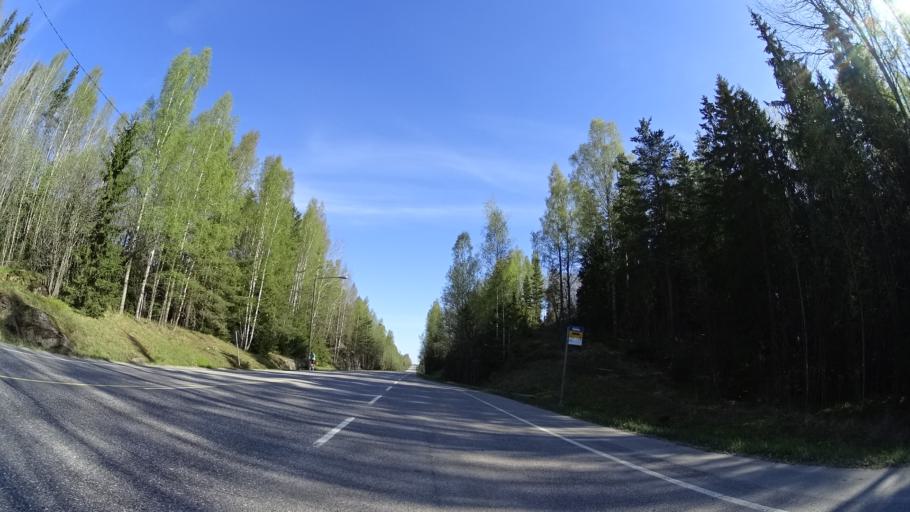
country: FI
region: Uusimaa
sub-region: Helsinki
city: Nurmijaervi
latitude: 60.3743
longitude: 24.8058
